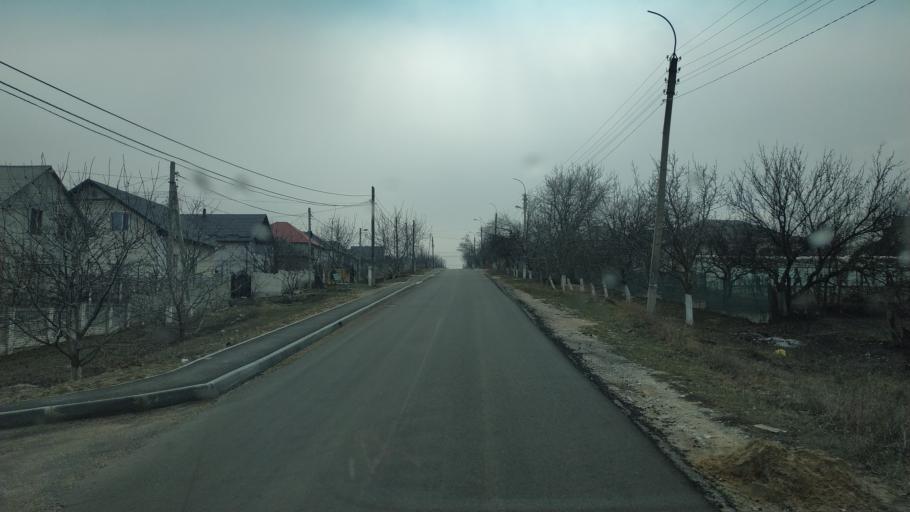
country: MD
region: Chisinau
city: Singera
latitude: 46.9096
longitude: 28.9870
